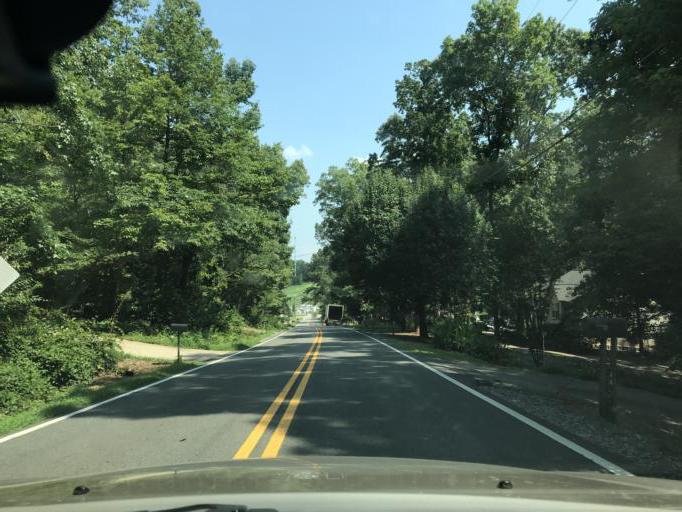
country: US
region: Georgia
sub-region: Hall County
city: Flowery Branch
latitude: 34.2474
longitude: -83.9977
